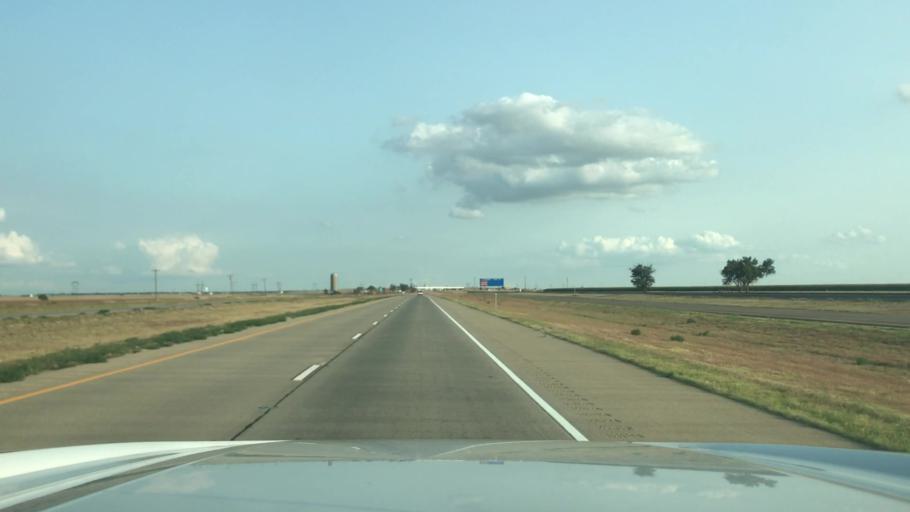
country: US
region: Texas
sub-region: Swisher County
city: Tulia
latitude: 34.5935
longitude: -101.8021
